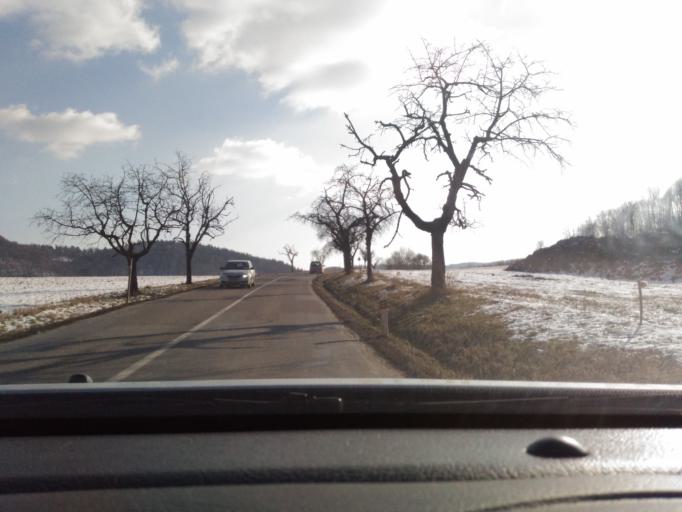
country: CZ
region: South Moravian
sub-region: Okres Brno-Venkov
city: Nedvedice
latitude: 49.4137
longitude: 16.3517
